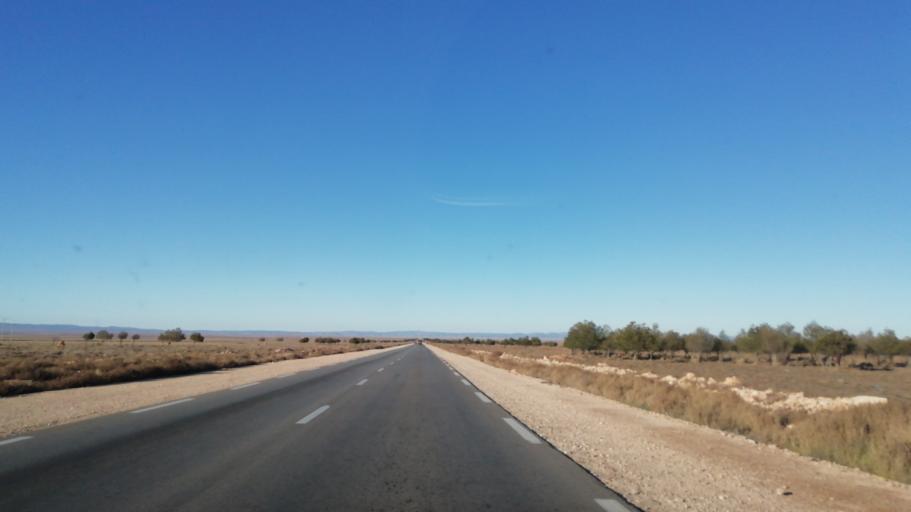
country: DZ
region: Tlemcen
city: Sebdou
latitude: 34.3263
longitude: -1.2638
